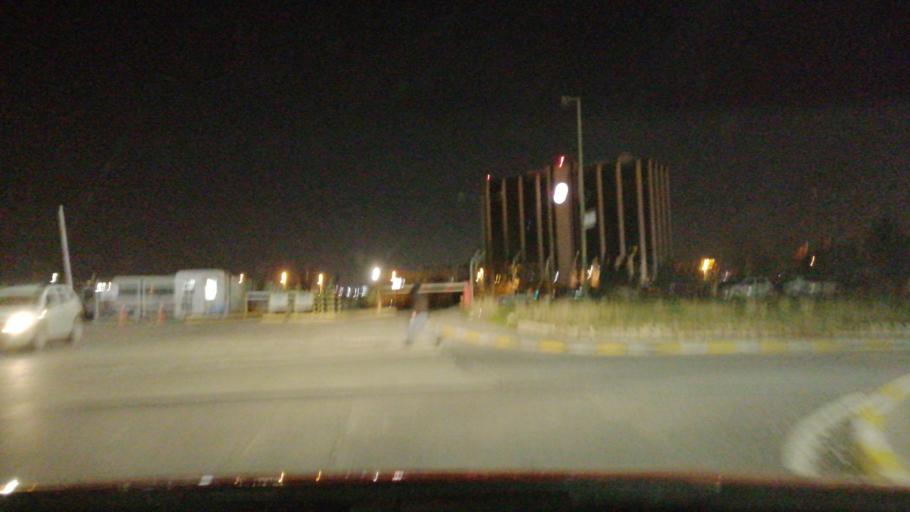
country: TR
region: Istanbul
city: Bahcelievler
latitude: 40.9803
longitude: 28.8248
